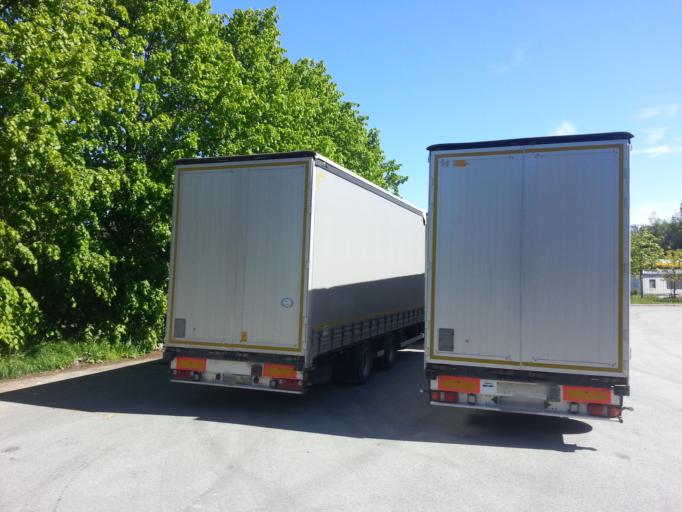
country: NO
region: Sor-Trondelag
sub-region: Malvik
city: Malvik
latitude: 63.4236
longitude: 10.7265
